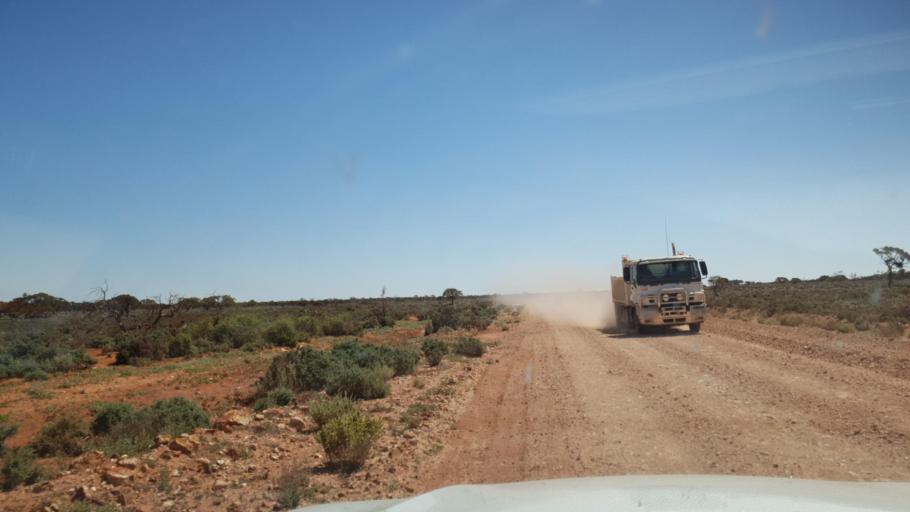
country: AU
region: South Australia
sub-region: Whyalla
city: Whyalla
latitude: -32.6577
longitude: 137.0447
